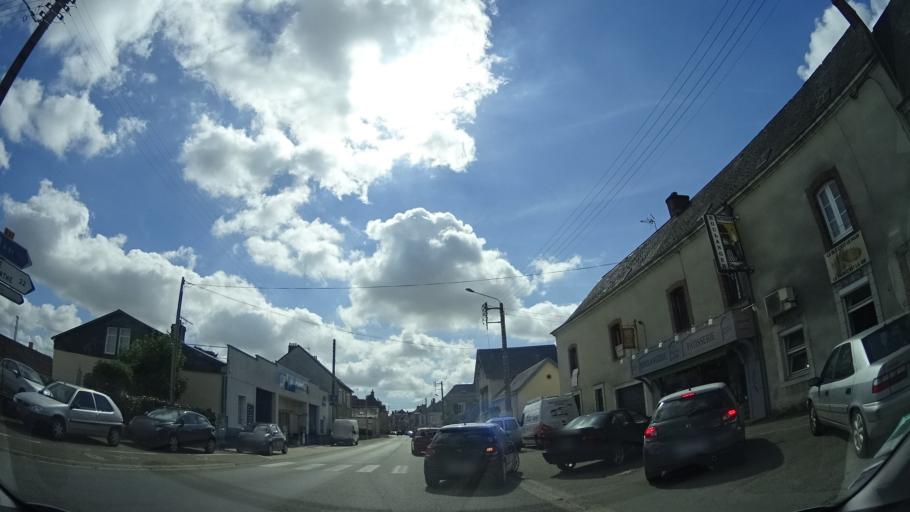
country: FR
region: Pays de la Loire
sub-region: Departement de la Mayenne
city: Meslay-du-Maine
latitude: 47.9517
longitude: -0.5566
